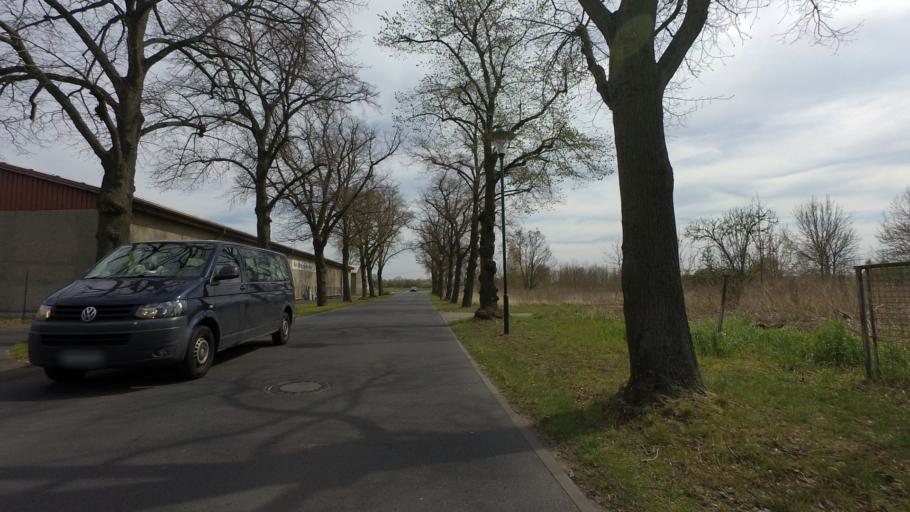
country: DE
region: Berlin
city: Lichtenrade
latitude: 52.3793
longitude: 13.4474
